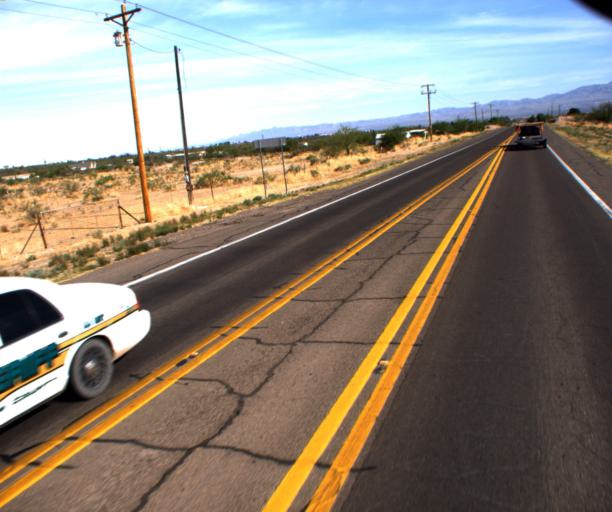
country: US
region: Arizona
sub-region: Graham County
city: Cactus Flat
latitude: 32.7525
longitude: -109.7163
